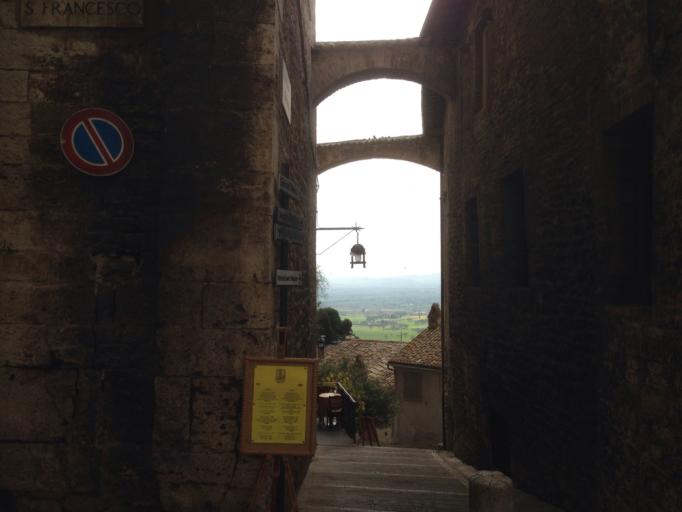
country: IT
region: Umbria
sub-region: Provincia di Perugia
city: Assisi
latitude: 43.0722
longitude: 12.6115
